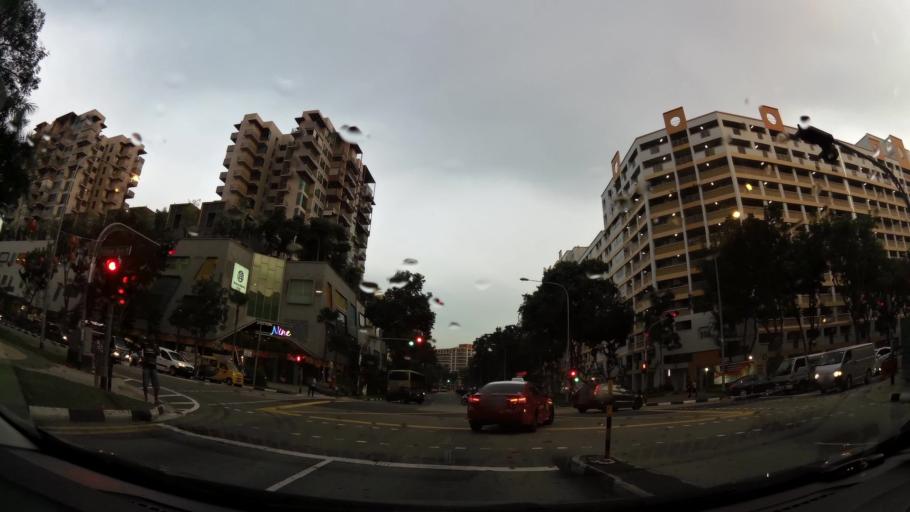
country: MY
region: Johor
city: Kampung Pasir Gudang Baru
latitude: 1.4332
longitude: 103.8407
